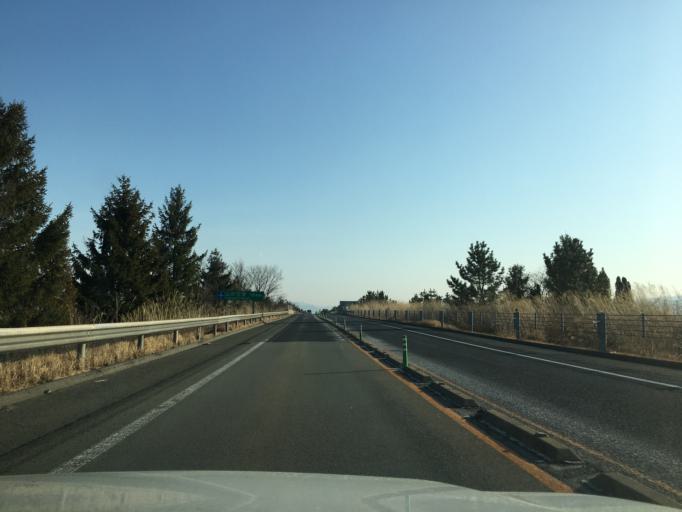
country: JP
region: Yamagata
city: Sagae
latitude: 38.3408
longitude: 140.2972
